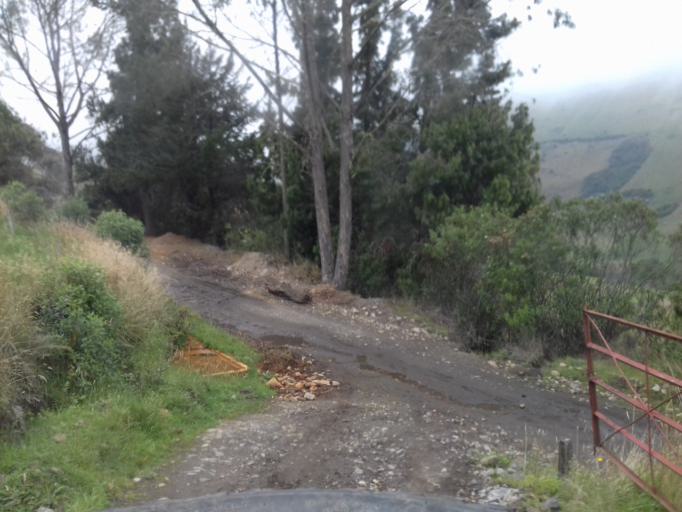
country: CO
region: Tolima
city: Murillo
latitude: 4.8962
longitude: -75.2371
